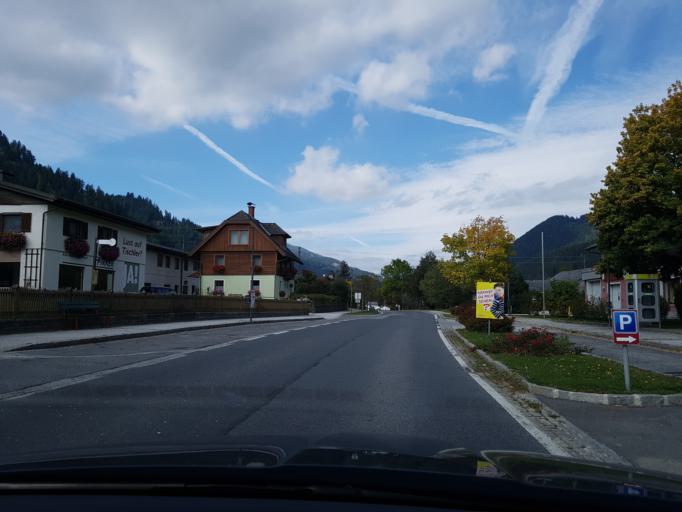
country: AT
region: Carinthia
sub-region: Politischer Bezirk Feldkirchen
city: Gnesau
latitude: 46.7753
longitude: 13.9634
